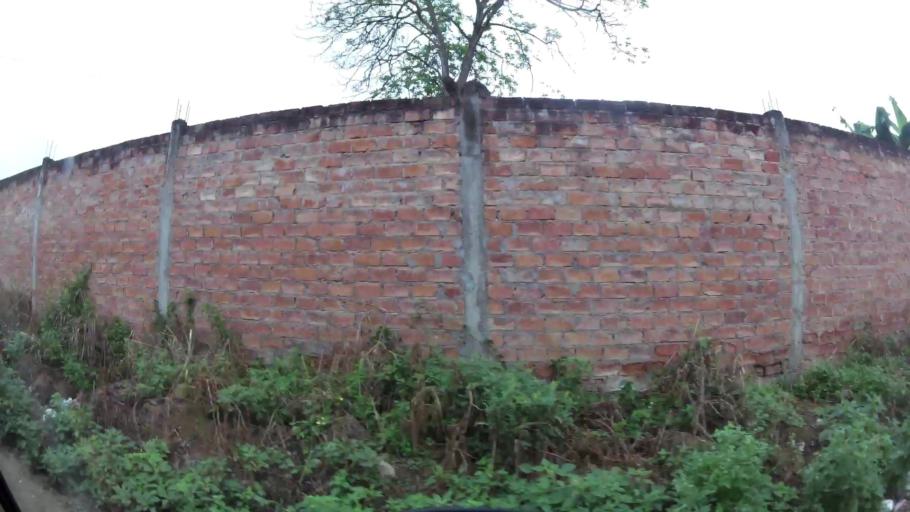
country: EC
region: El Oro
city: Pasaje
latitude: -3.3215
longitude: -79.8099
